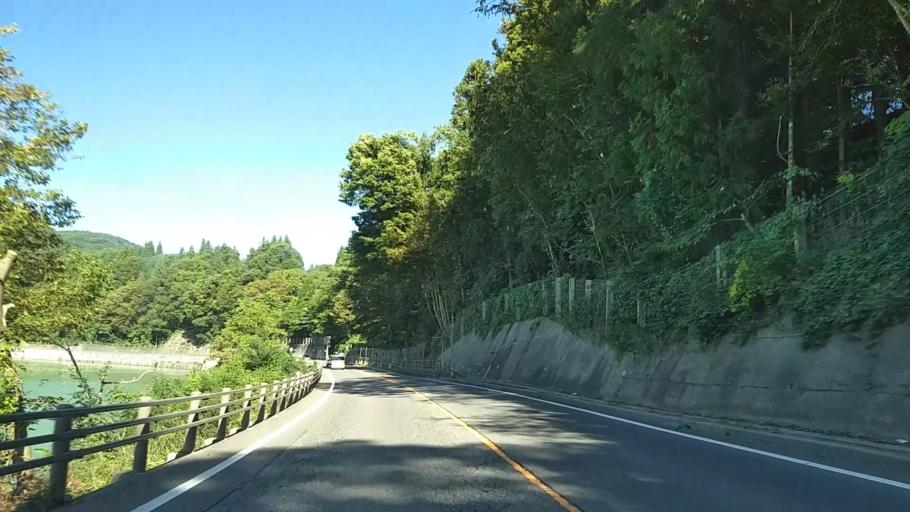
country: JP
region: Nagano
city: Nagano-shi
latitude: 36.6164
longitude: 138.1010
